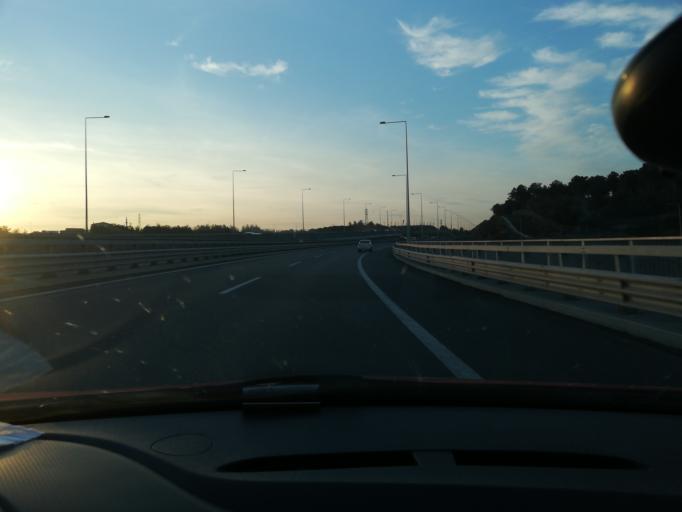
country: TR
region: Istanbul
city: Umraniye
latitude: 41.0499
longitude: 29.1266
